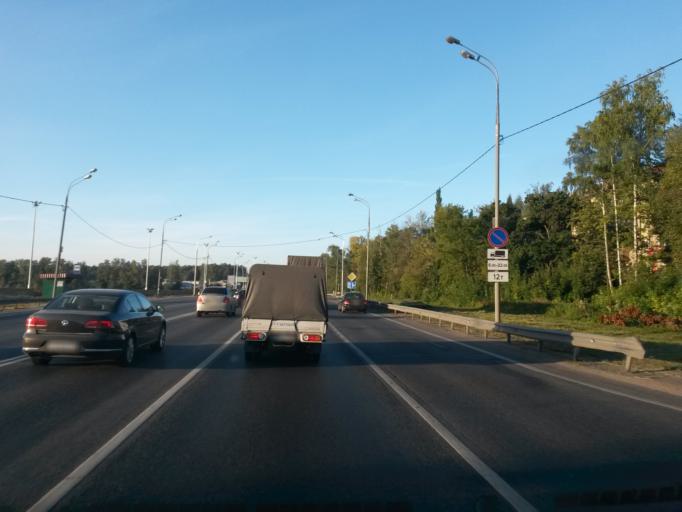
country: RU
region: Moskovskaya
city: Bolshevo
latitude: 55.9486
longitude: 37.8149
